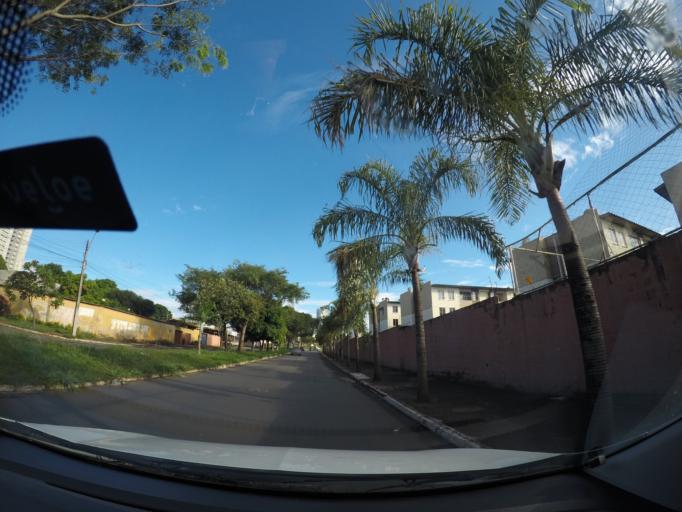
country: BR
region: Goias
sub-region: Goiania
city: Goiania
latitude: -16.7490
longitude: -49.2747
